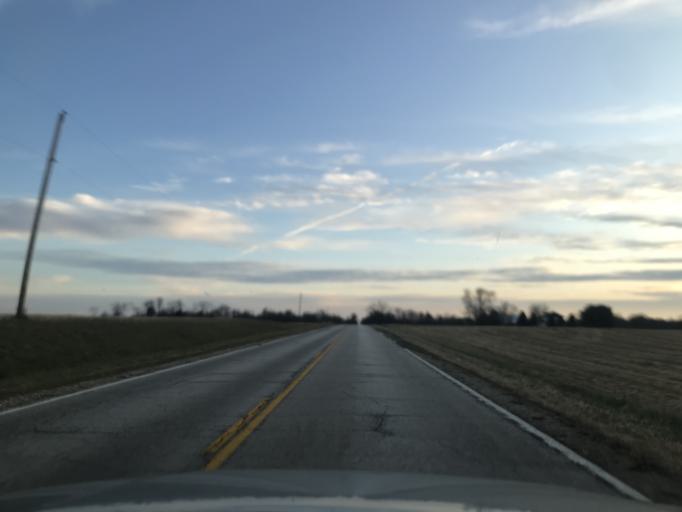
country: US
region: Illinois
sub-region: Henderson County
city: Oquawka
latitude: 40.9658
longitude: -90.8639
